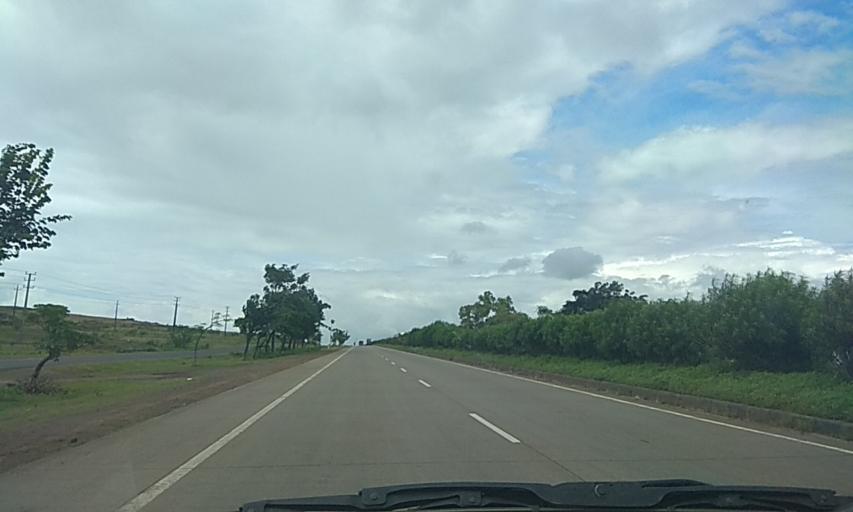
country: IN
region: Maharashtra
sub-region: Kolhapur
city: Kagal
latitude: 16.5209
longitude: 74.3260
